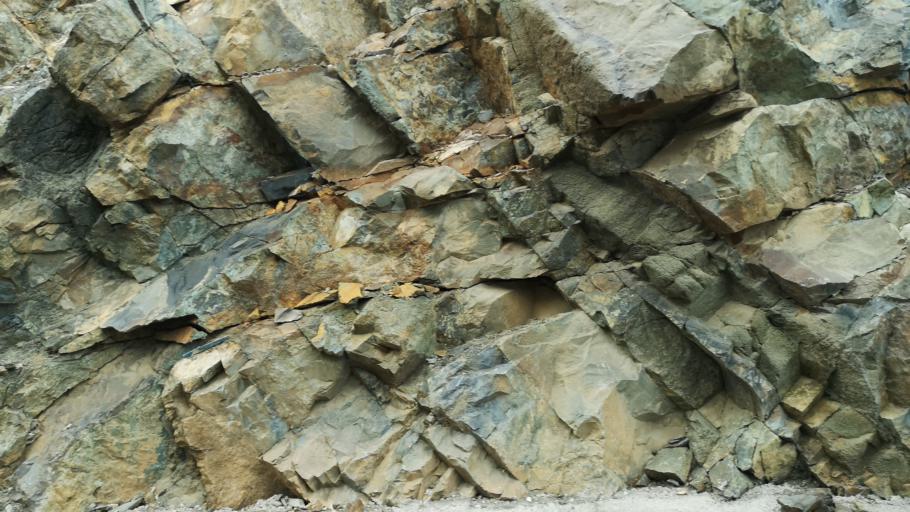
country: ES
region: Canary Islands
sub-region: Provincia de Santa Cruz de Tenerife
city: Vallehermosa
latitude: 28.1999
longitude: -17.2564
